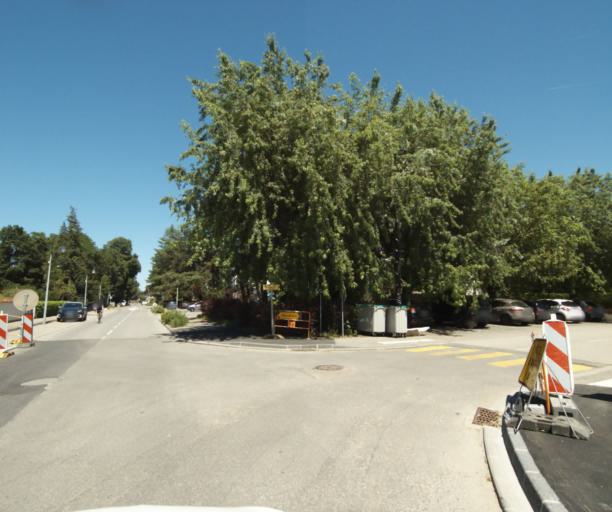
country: FR
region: Rhone-Alpes
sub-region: Departement de la Haute-Savoie
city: Veigy-Foncenex
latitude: 46.2719
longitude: 6.2583
